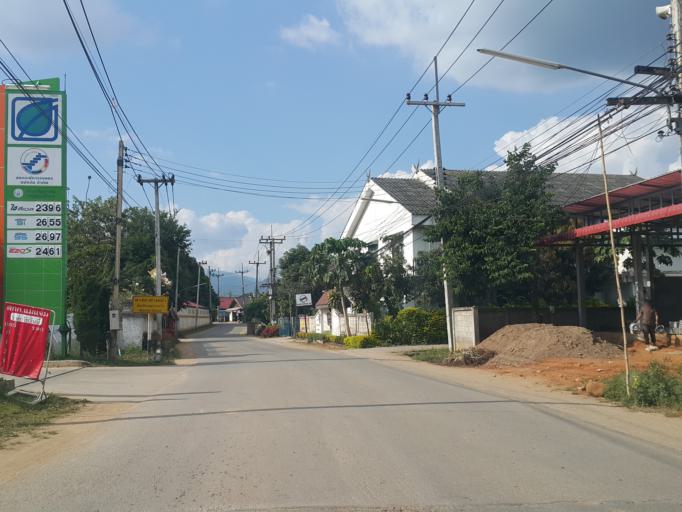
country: TH
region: Chiang Mai
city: Mae Chaem
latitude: 18.5095
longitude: 98.3598
